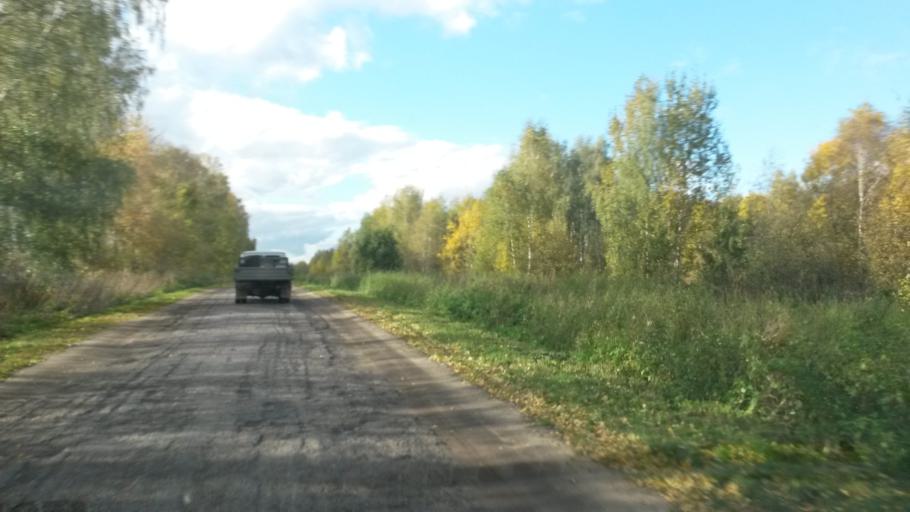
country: RU
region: Jaroslavl
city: Tunoshna
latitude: 57.5247
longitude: 40.0081
